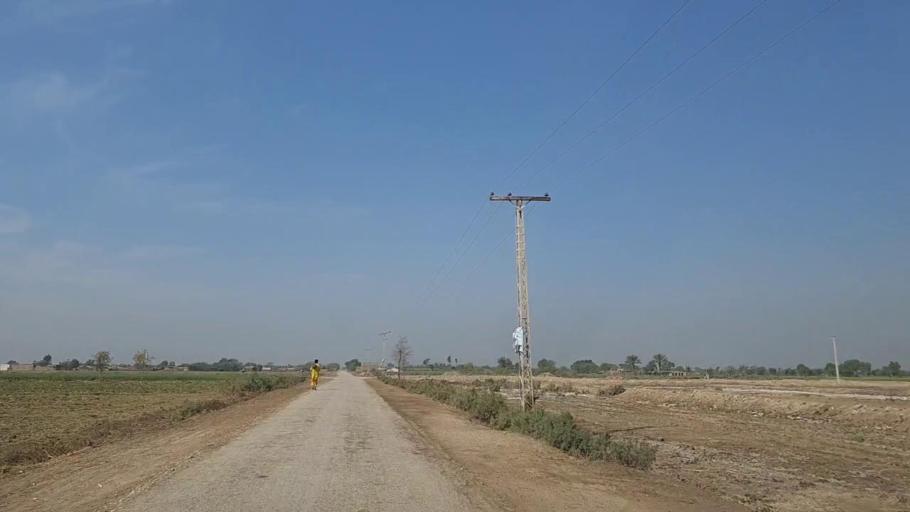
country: PK
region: Sindh
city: Mirpur Khas
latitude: 25.4825
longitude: 68.9931
